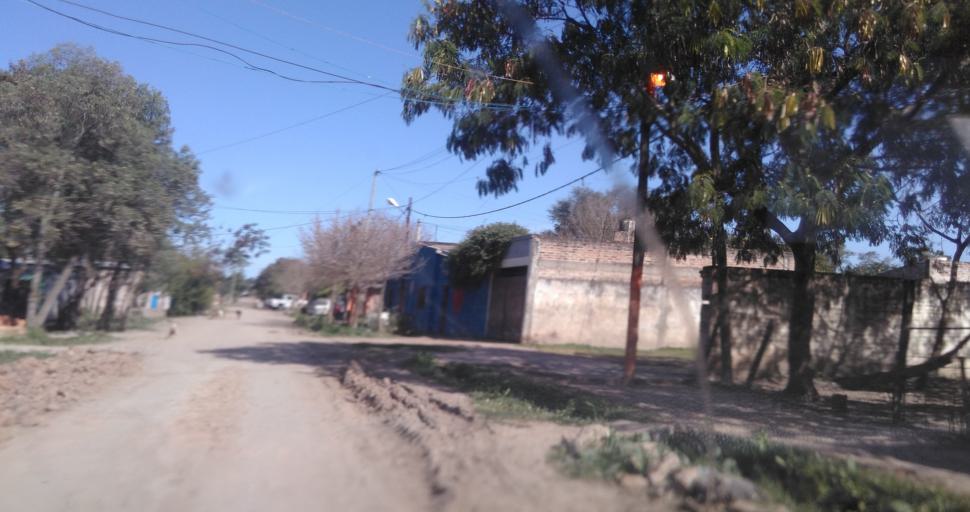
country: AR
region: Chaco
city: Fontana
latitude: -27.4354
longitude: -59.0238
